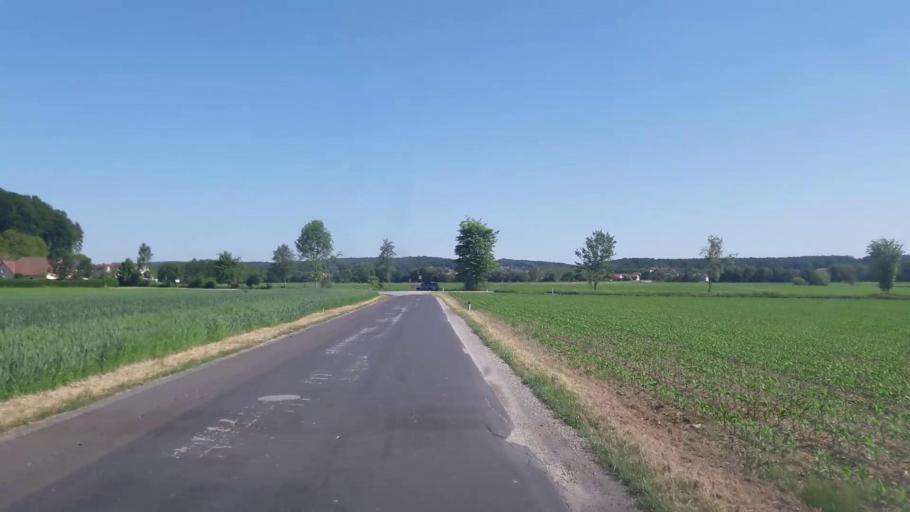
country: AT
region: Styria
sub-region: Politischer Bezirk Hartberg-Fuerstenfeld
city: UEbersbach
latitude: 47.0119
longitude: 16.0499
